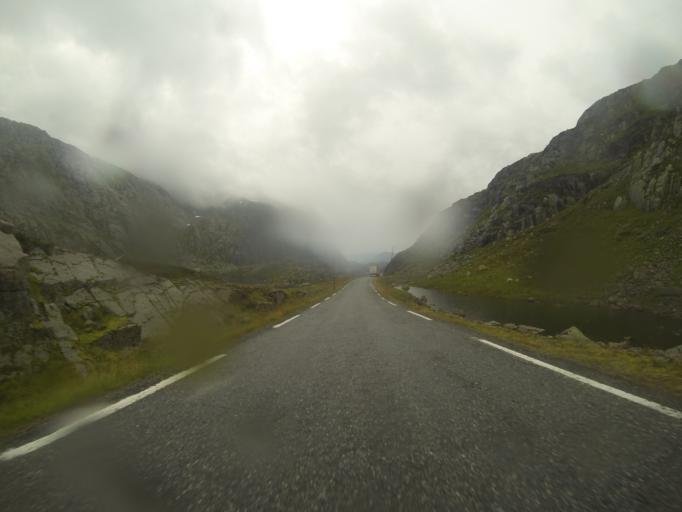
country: NO
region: Hordaland
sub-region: Odda
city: Odda
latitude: 59.7601
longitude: 6.7175
